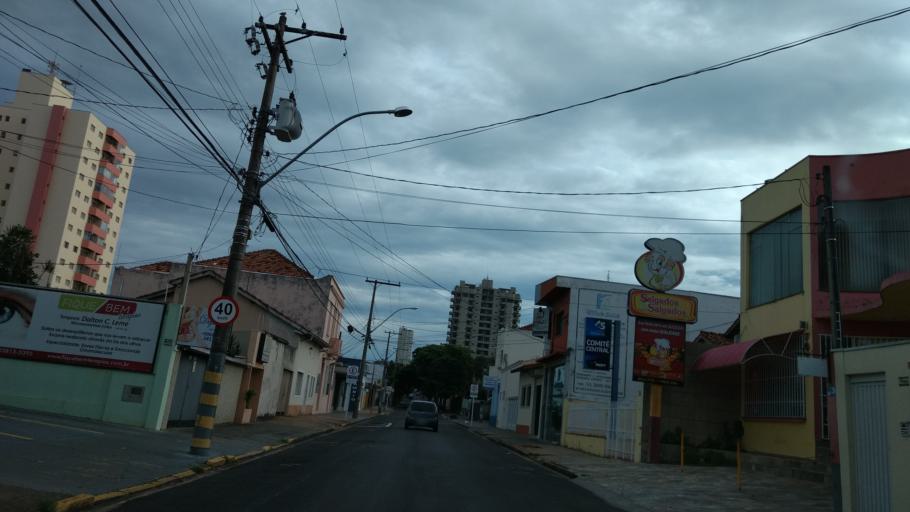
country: BR
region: Sao Paulo
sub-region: Botucatu
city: Botucatu
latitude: -22.8858
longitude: -48.4426
